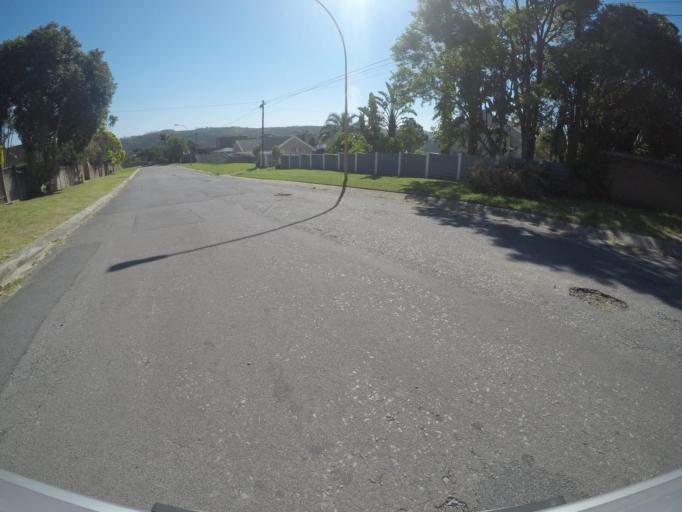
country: ZA
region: Eastern Cape
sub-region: Buffalo City Metropolitan Municipality
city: East London
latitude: -32.9504
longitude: 27.9001
